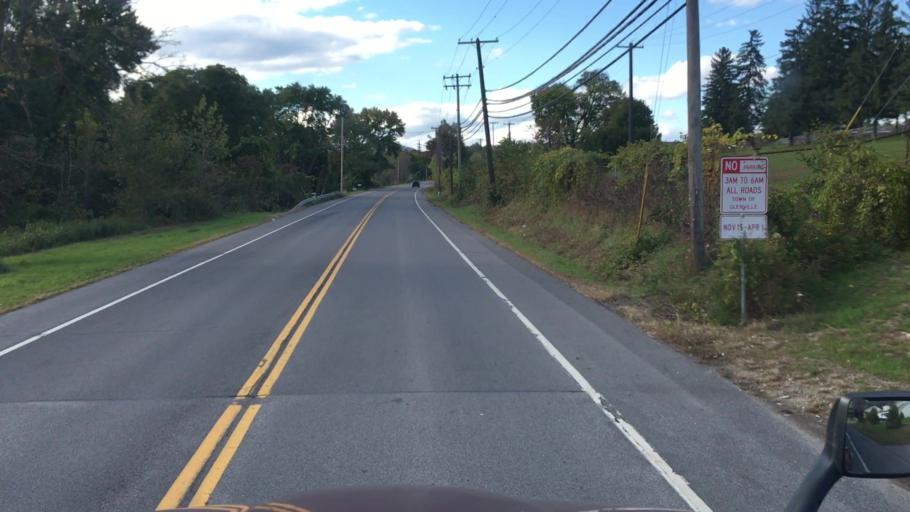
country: US
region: New York
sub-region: Schenectady County
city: Scotia
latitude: 42.8319
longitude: -73.9807
